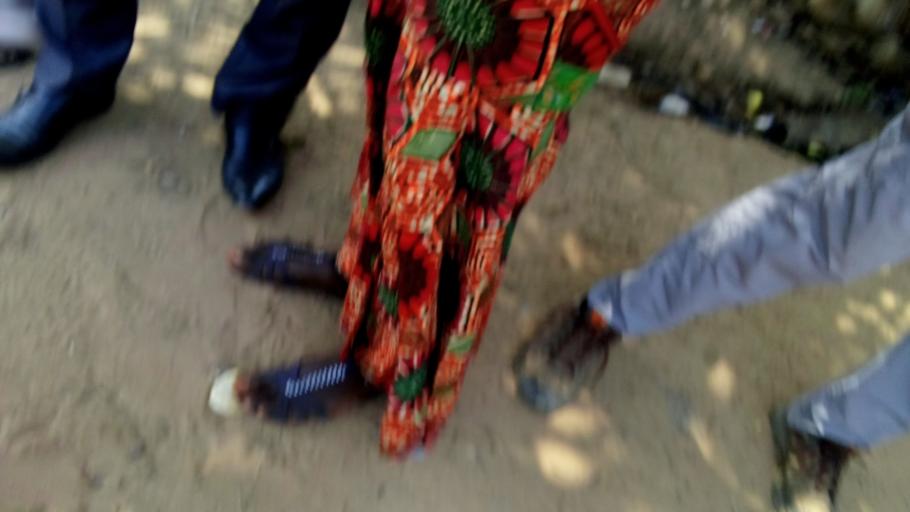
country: GN
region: Kindia
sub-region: Prefecture de Dubreka
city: Dubreka
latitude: 9.7833
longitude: -13.5220
